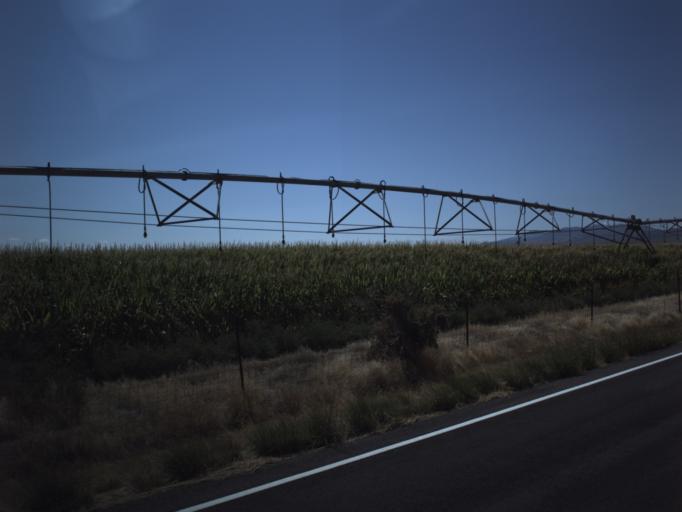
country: US
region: Utah
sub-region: Utah County
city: Genola
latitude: 40.1297
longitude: -111.9539
